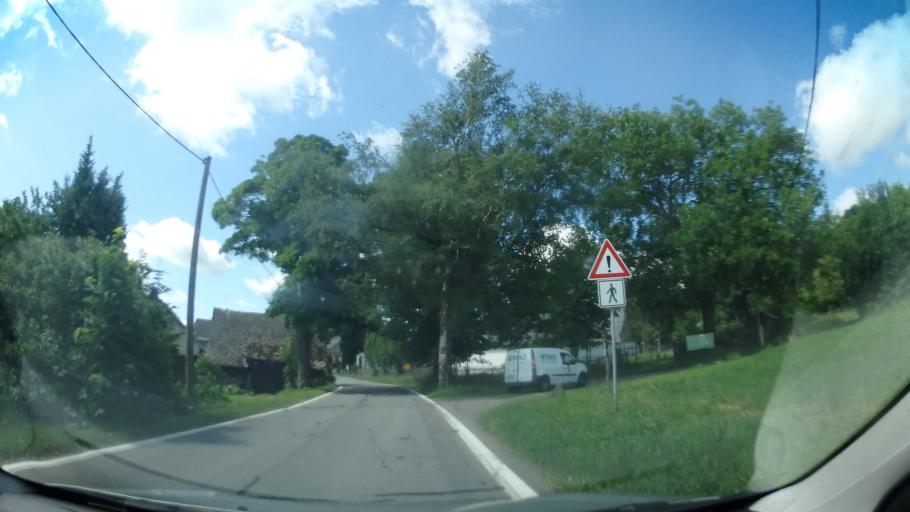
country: CZ
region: Vysocina
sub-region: Okres Zd'ar nad Sazavou
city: Nove Mesto na Morave
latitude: 49.6424
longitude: 16.0973
